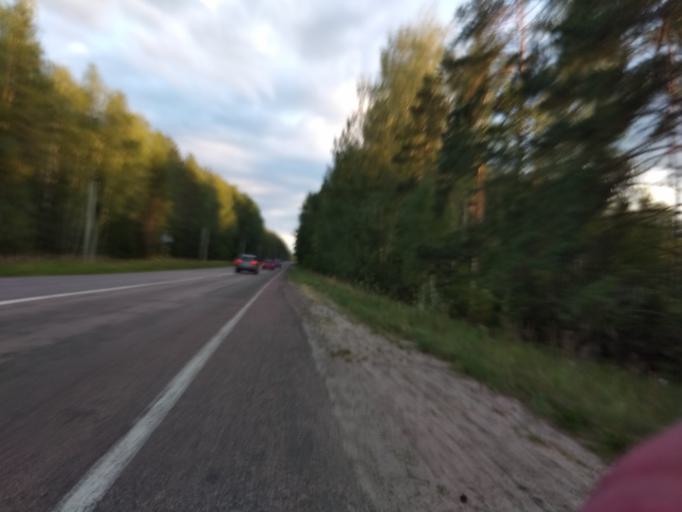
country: RU
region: Moskovskaya
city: Misheronskiy
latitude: 55.6172
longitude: 39.7246
